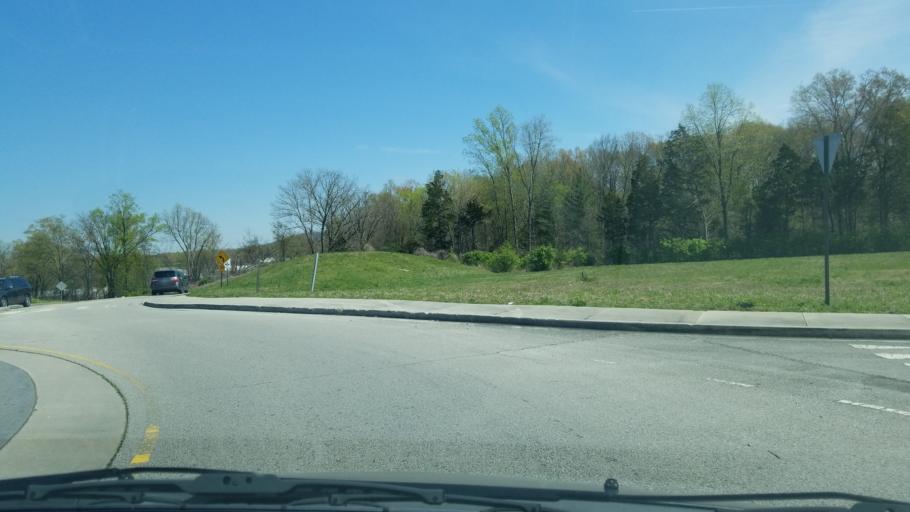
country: US
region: Tennessee
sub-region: Hamilton County
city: Red Bank
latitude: 35.1286
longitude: -85.2351
